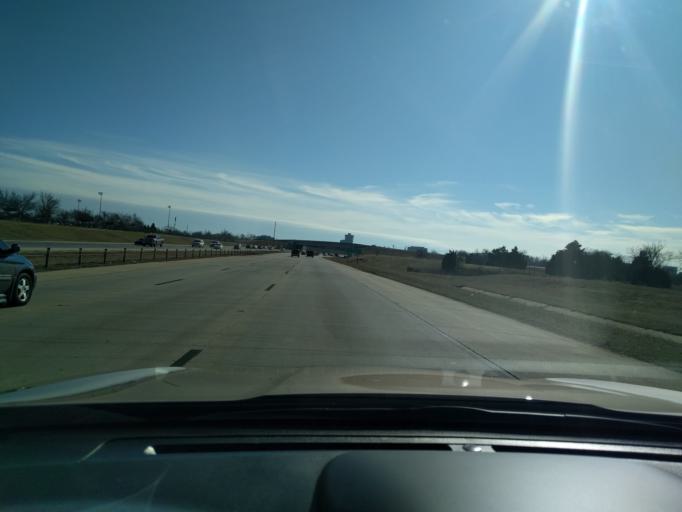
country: US
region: Oklahoma
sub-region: Oklahoma County
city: Nichols Hills
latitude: 35.5478
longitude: -97.5766
